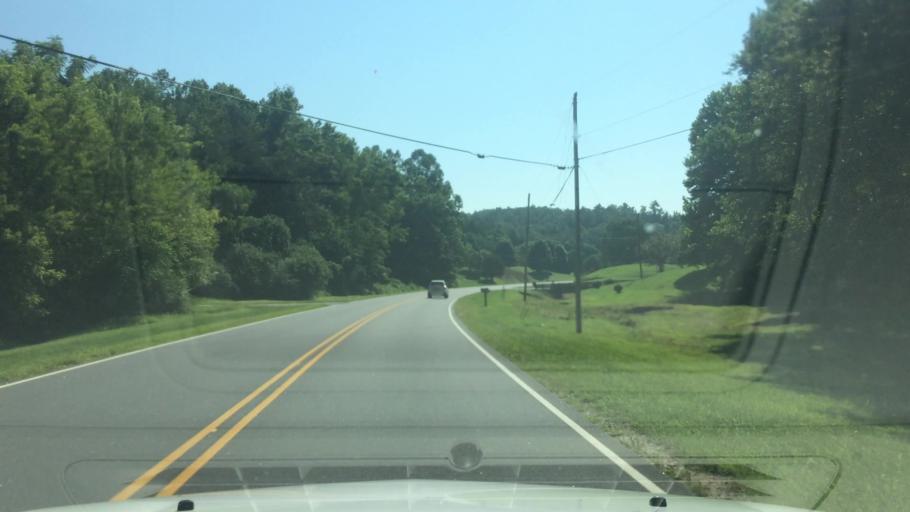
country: US
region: North Carolina
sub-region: Caldwell County
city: Hudson
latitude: 35.9181
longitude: -81.4613
